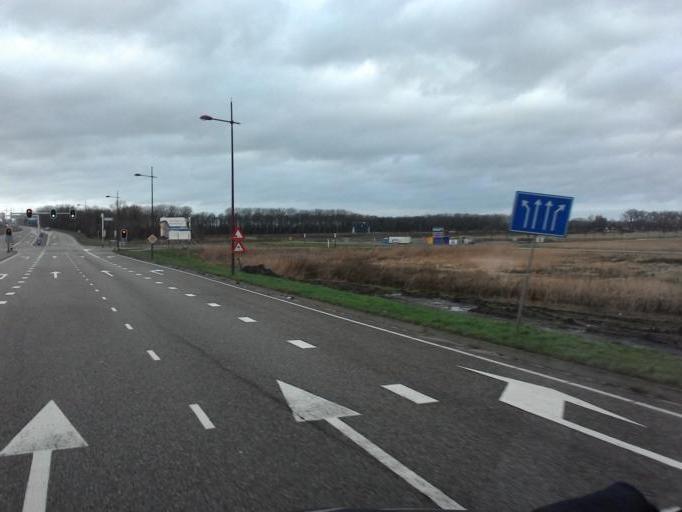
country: NL
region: Utrecht
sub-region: Gemeente Vianen
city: Vianen
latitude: 52.0138
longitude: 5.1166
